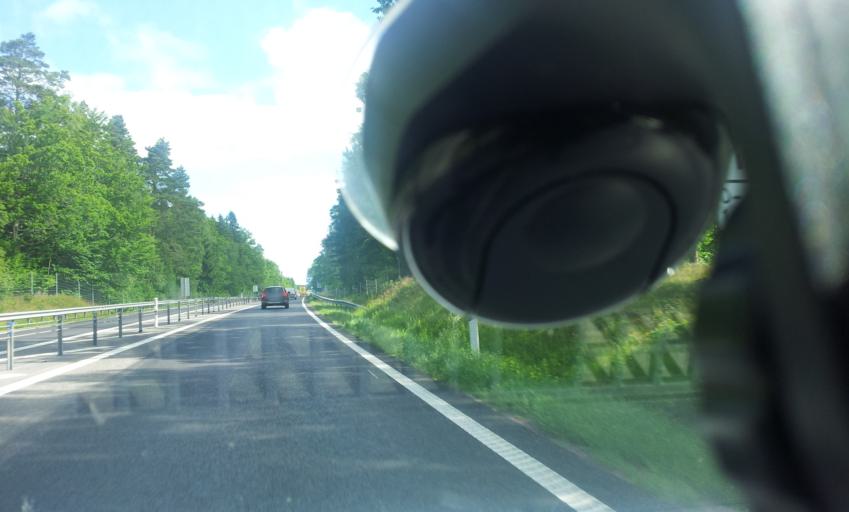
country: SE
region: Kalmar
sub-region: Monsteras Kommun
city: Timmernabben
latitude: 56.9042
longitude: 16.3794
